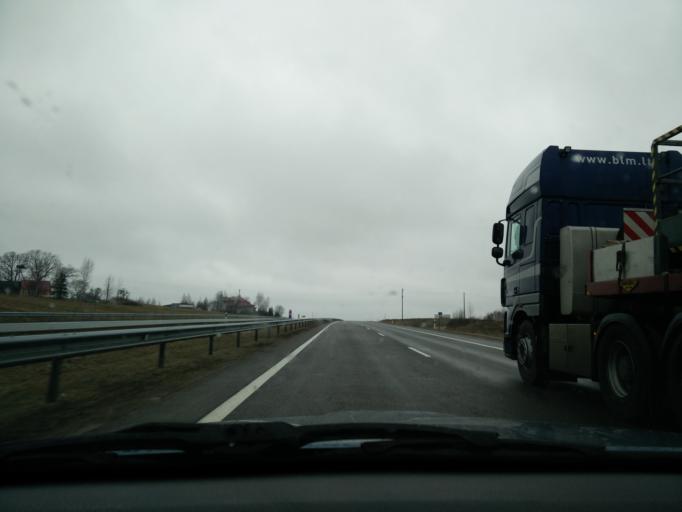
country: LT
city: Silale
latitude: 55.5193
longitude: 22.3718
